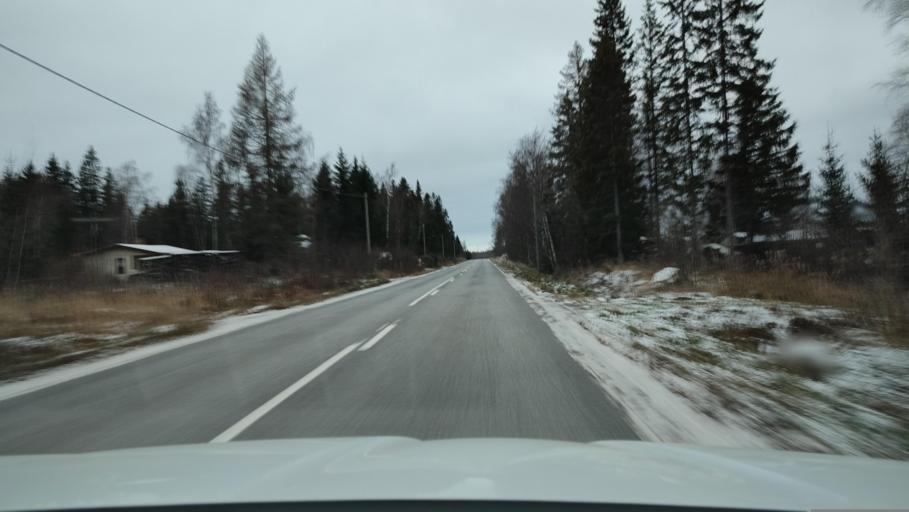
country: FI
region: Ostrobothnia
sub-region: Vaasa
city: Replot
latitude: 63.2676
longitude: 21.3480
